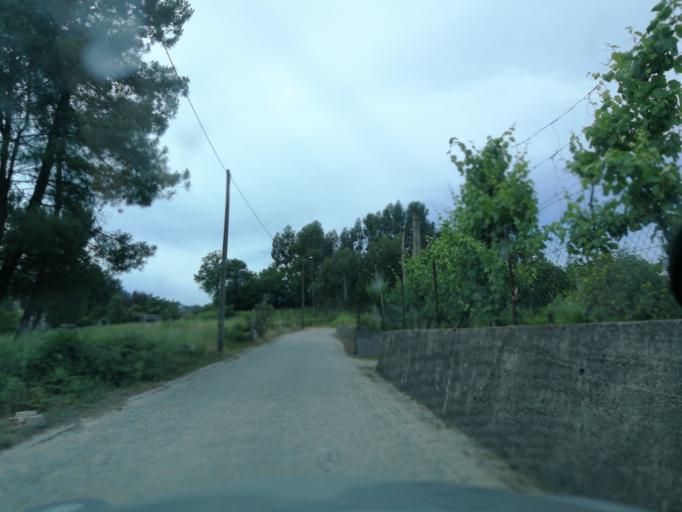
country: PT
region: Braga
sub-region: Braga
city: Oliveira
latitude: 41.4777
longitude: -8.4808
